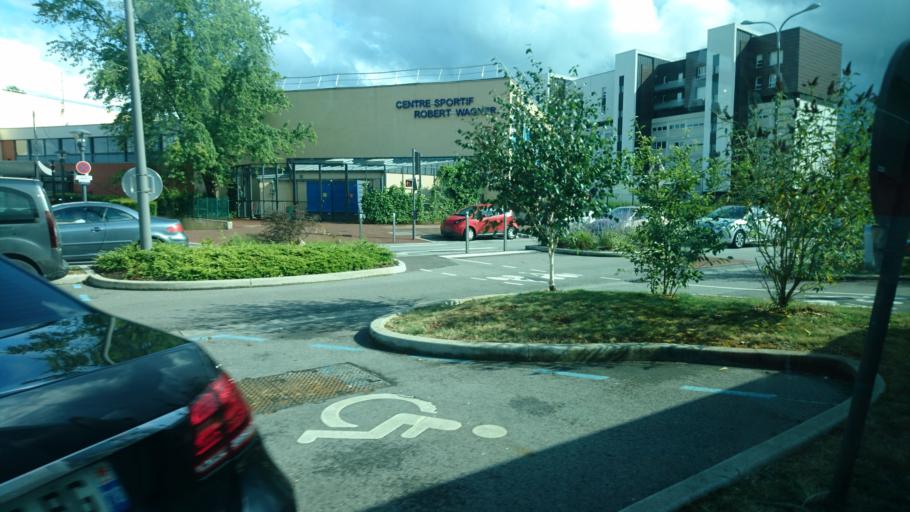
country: FR
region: Ile-de-France
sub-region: Departement des Yvelines
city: Velizy-Villacoublay
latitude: 48.7844
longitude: 2.1776
